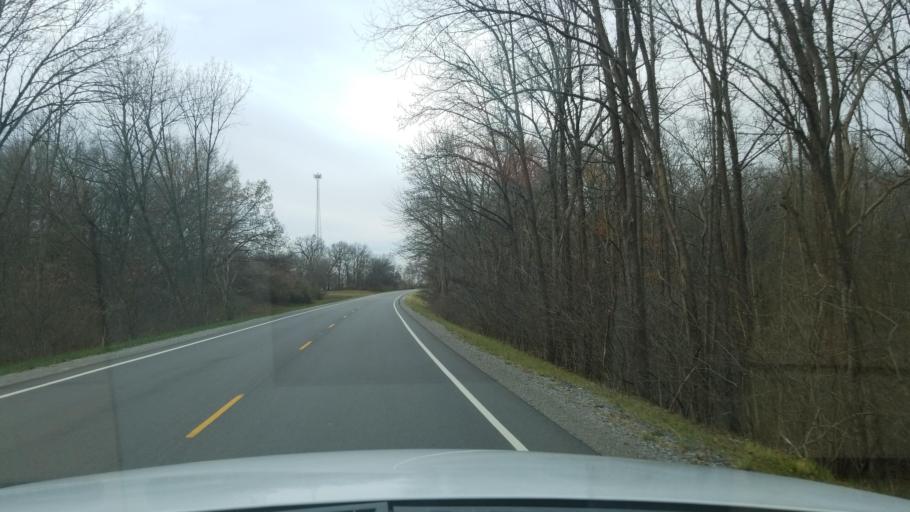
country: US
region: Illinois
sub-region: White County
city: Carmi
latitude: 37.9102
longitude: -88.1329
